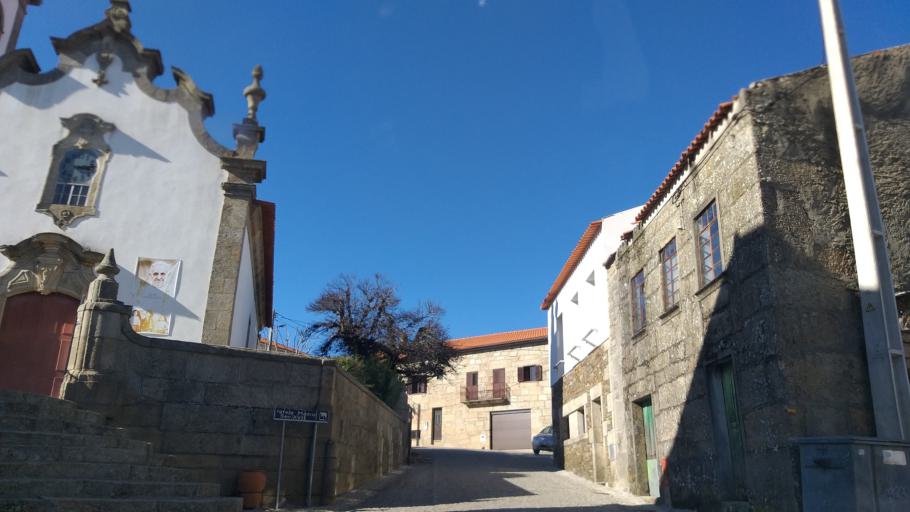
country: PT
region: Guarda
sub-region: Celorico da Beira
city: Celorico da Beira
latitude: 40.5147
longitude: -7.3930
